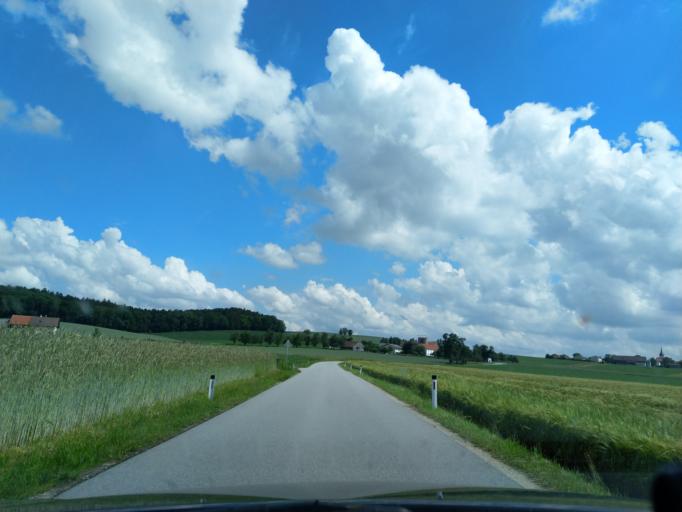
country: DE
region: Bavaria
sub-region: Lower Bavaria
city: Bad Fussing
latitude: 48.3119
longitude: 13.3618
